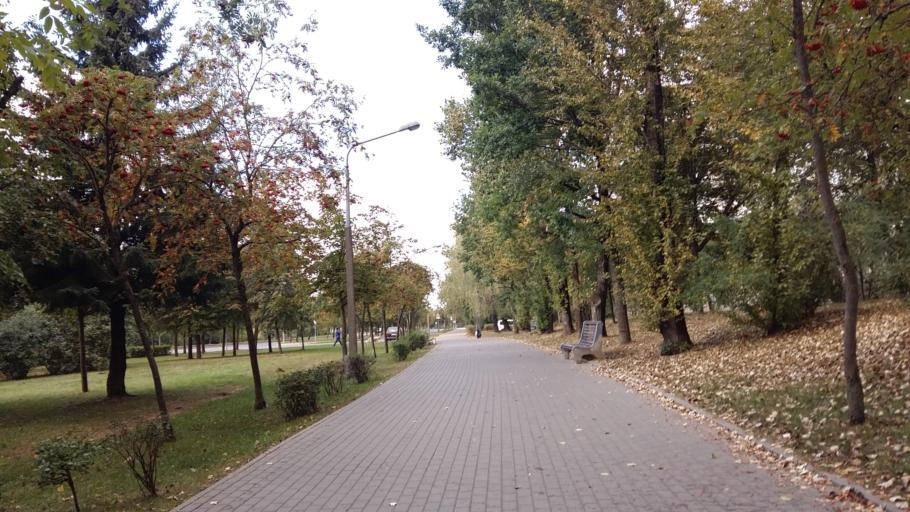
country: BY
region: Grodnenskaya
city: Hrodna
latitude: 53.6995
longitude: 23.7996
